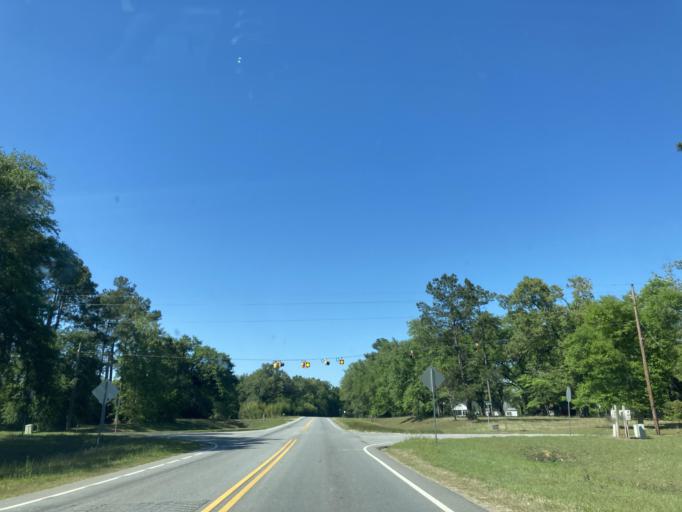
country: US
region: Georgia
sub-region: Baker County
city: Newton
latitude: 31.3151
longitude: -84.3475
